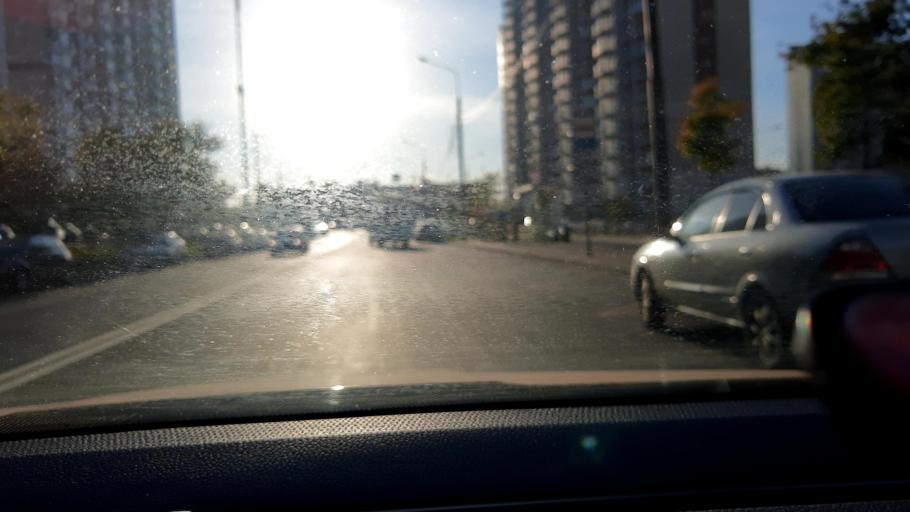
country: RU
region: Moskovskaya
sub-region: Leninskiy Rayon
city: Vnukovo
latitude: 55.6236
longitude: 37.3044
